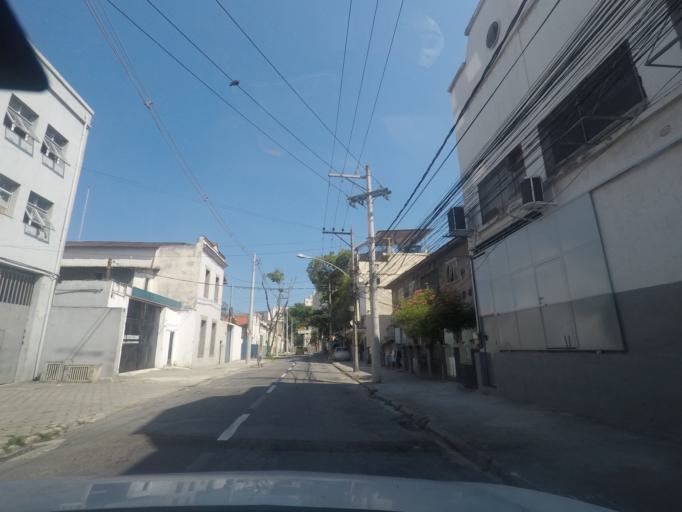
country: BR
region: Rio de Janeiro
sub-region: Rio De Janeiro
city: Rio de Janeiro
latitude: -22.8906
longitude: -43.2214
